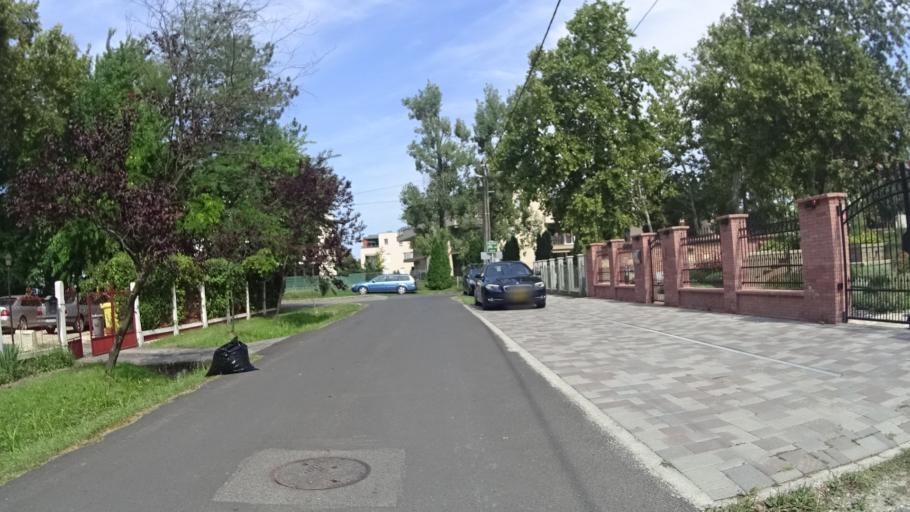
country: HU
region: Somogy
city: Balatonboglar
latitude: 46.7731
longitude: 17.6331
